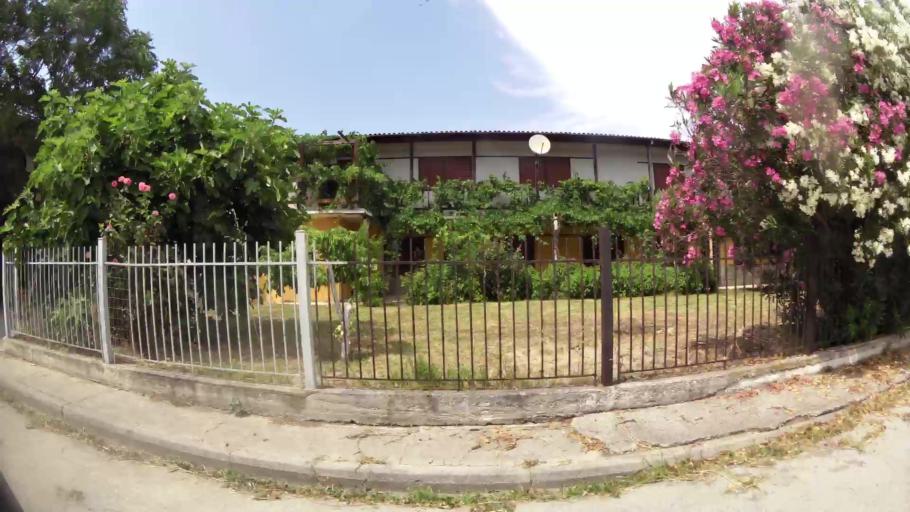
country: GR
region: Central Macedonia
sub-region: Nomos Pierias
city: Korinos
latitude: 40.3123
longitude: 22.5942
